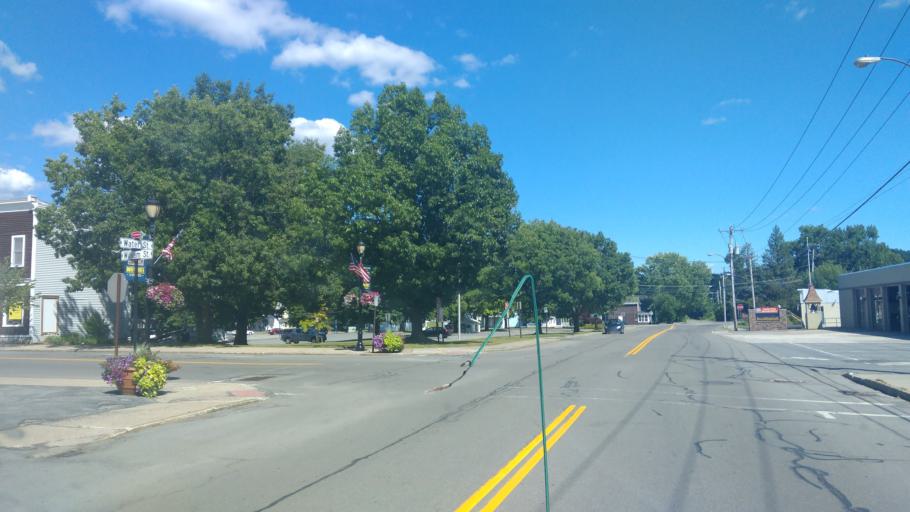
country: US
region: New York
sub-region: Wayne County
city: Lyons
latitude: 43.0622
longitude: -76.9934
